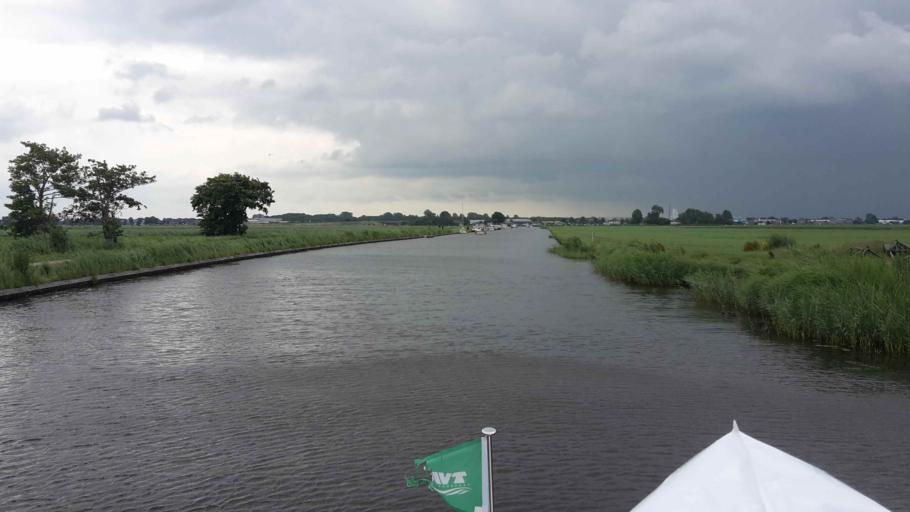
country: NL
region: Overijssel
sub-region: Gemeente Steenwijkerland
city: Steenwijkerwold
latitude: 52.7888
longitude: 6.0711
